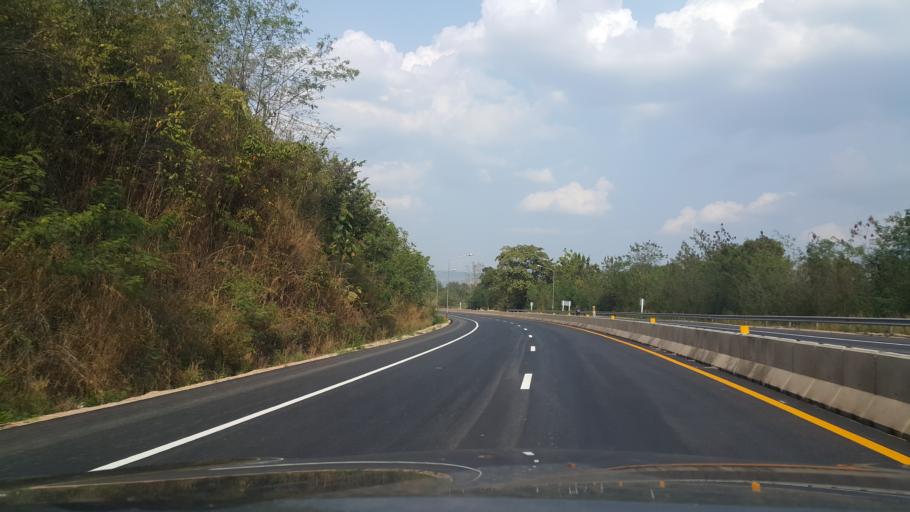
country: TH
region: Phitsanulok
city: Wang Thong
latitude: 16.8850
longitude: 100.6593
